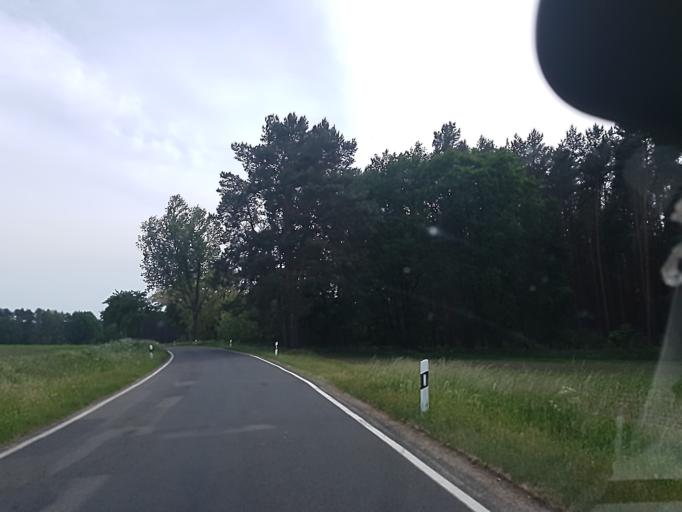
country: DE
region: Brandenburg
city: Belzig
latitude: 52.0535
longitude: 12.5712
